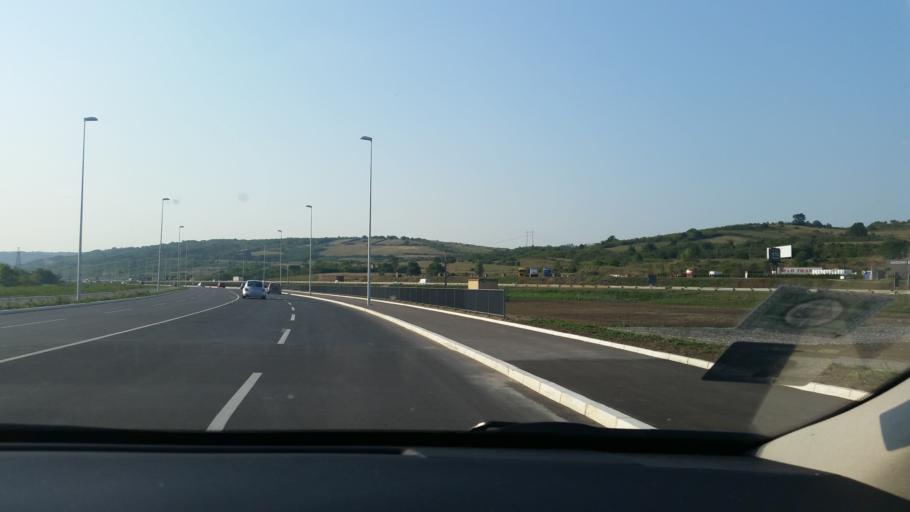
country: RS
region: Central Serbia
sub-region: Belgrade
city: Zvezdara
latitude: 44.7038
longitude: 20.5725
